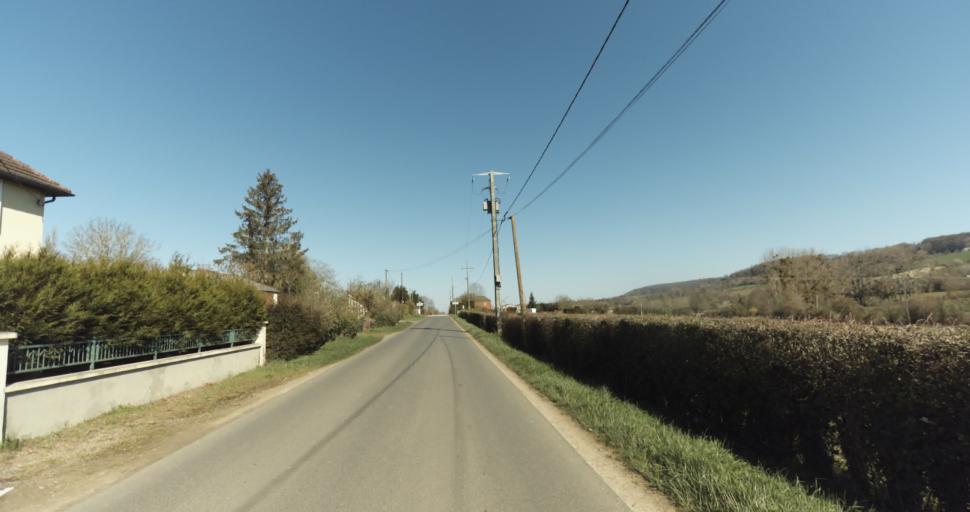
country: FR
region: Lower Normandy
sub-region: Departement du Calvados
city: Saint-Pierre-sur-Dives
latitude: 48.9772
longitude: 0.0361
